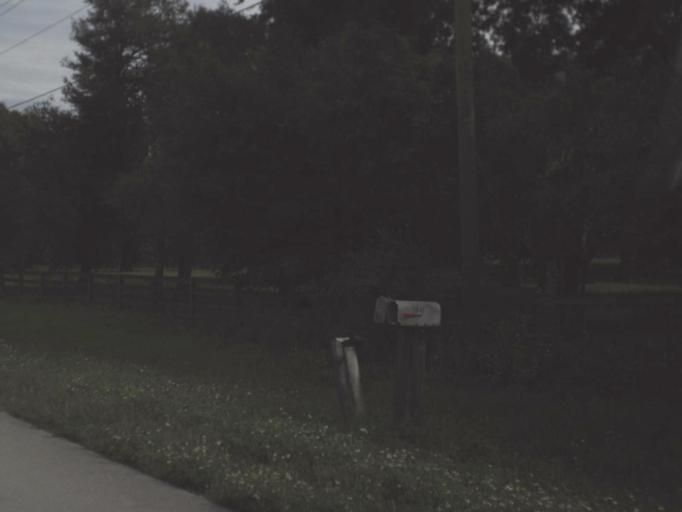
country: US
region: Florida
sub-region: DeSoto County
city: Southeast Arcadia
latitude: 27.1837
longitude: -81.8281
